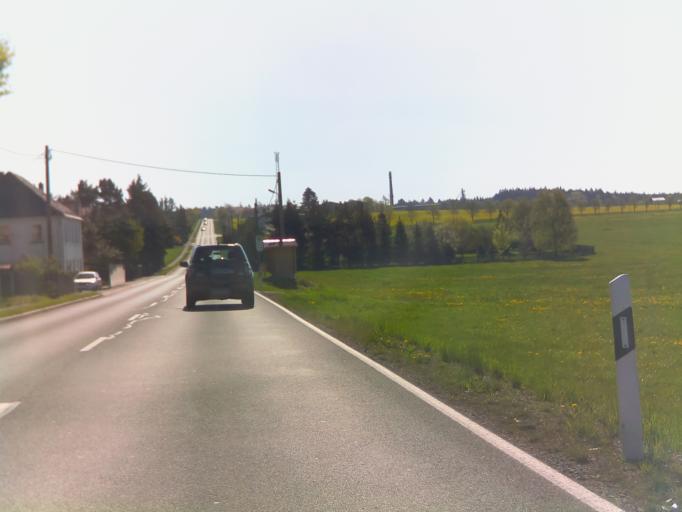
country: DE
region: Saxony
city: Mehltheuer
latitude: 50.5477
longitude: 12.0207
